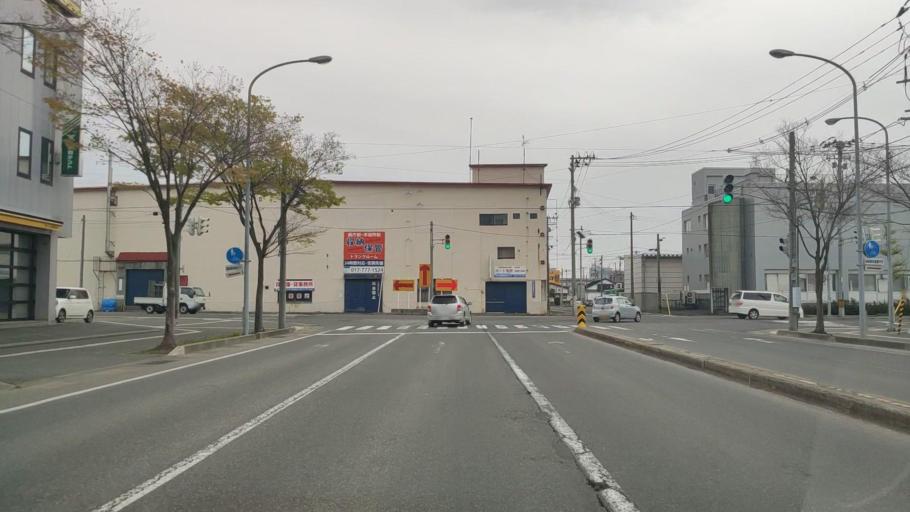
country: JP
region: Aomori
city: Aomori Shi
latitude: 40.8292
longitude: 140.7540
